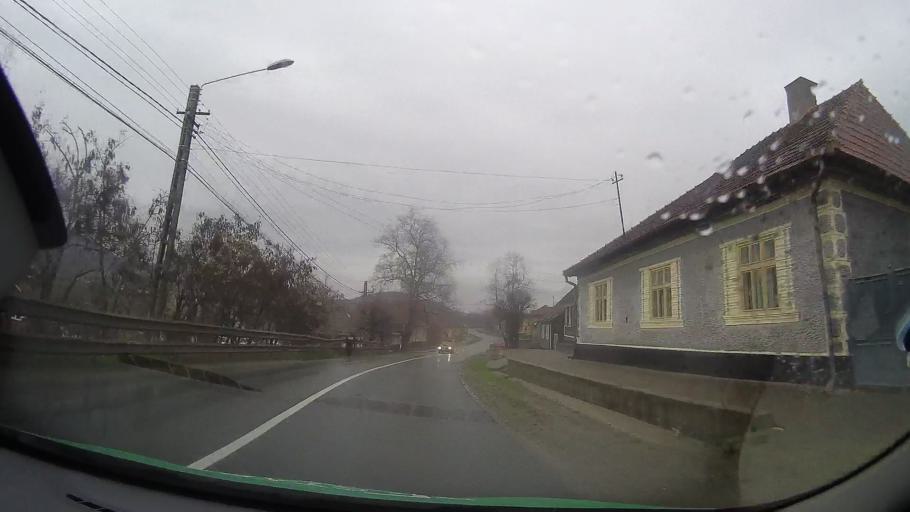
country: RO
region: Bistrita-Nasaud
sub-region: Municipiul Bistrita
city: Viisoara
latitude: 47.0730
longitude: 24.4350
